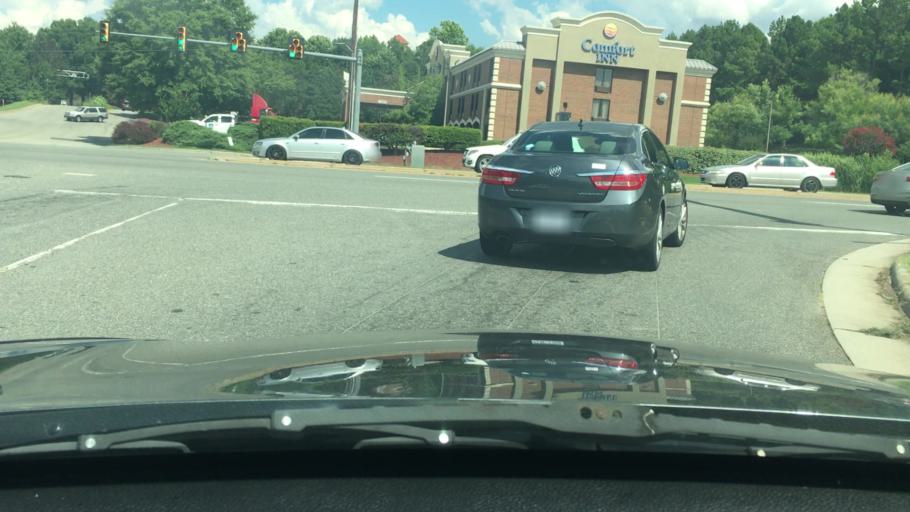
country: US
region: North Carolina
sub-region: Durham County
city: Durham
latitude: 35.9080
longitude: -78.8941
